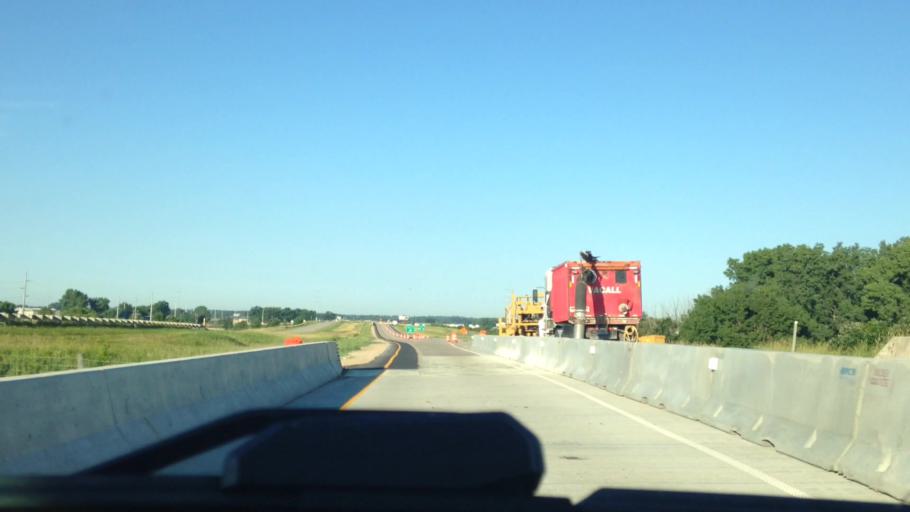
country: US
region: Wisconsin
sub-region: Columbia County
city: Columbus
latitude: 43.3522
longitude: -89.0281
